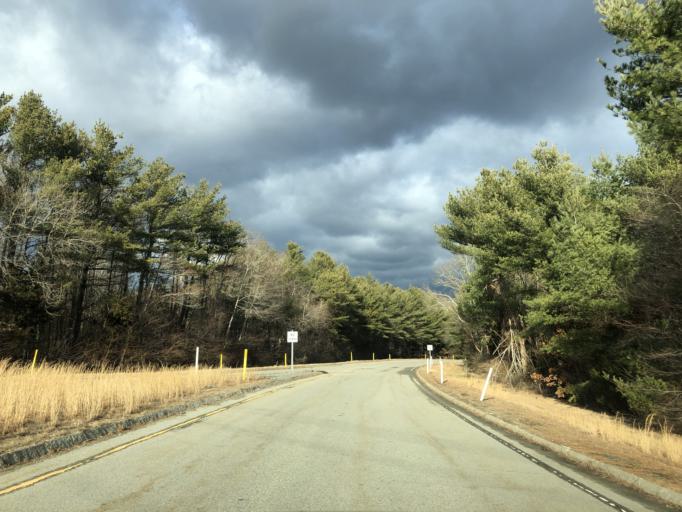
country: US
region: Massachusetts
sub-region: Plymouth County
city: Marion Center
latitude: 41.7258
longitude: -70.7763
